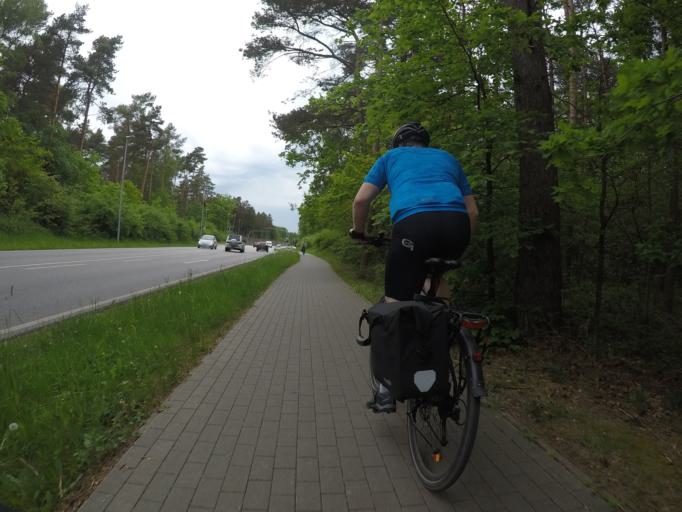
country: DE
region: Schleswig-Holstein
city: Norderstedt
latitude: 53.7162
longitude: 9.9803
